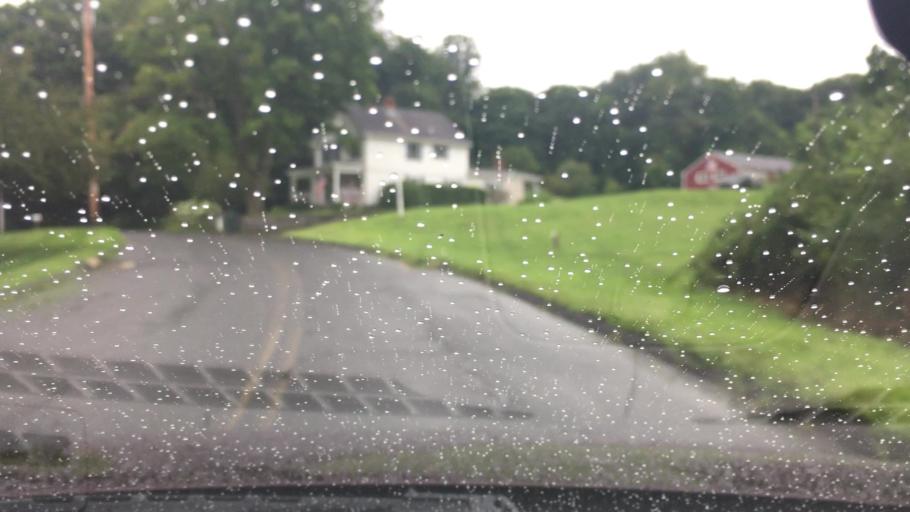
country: US
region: Connecticut
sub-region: New Haven County
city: Cheshire Village
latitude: 41.5458
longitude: -72.9275
